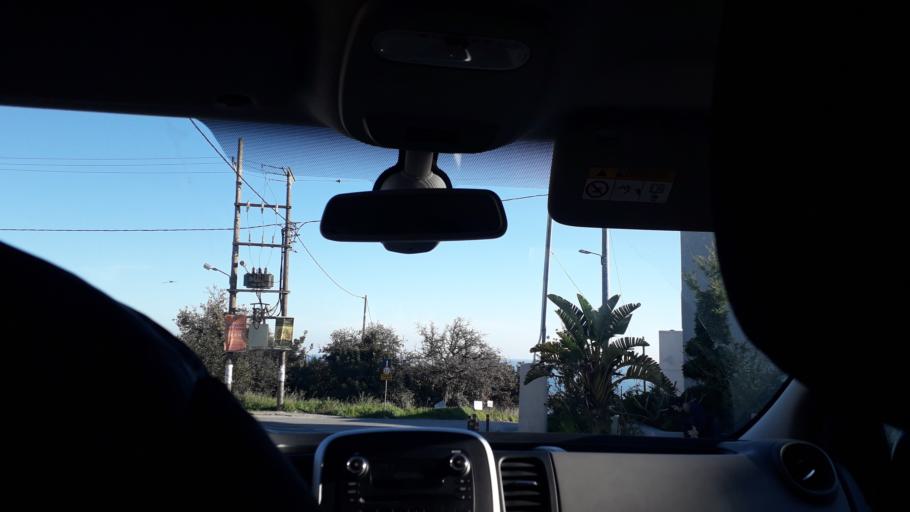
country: GR
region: Crete
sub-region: Nomos Rethymnis
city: Atsipopoulon
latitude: 35.3582
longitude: 24.4409
